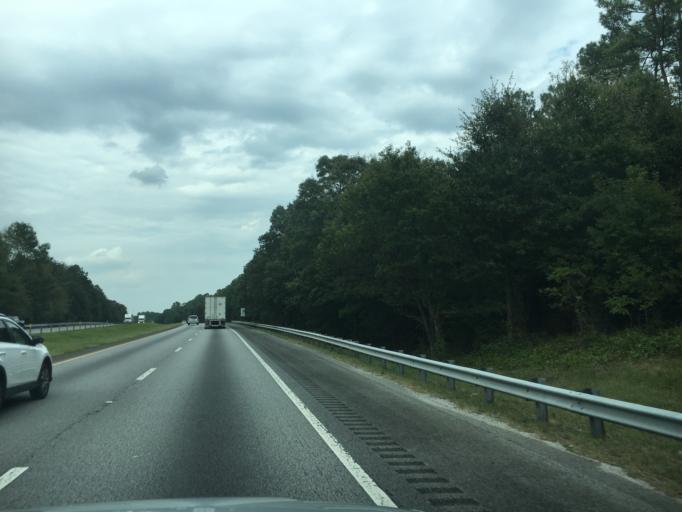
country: US
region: Georgia
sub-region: Hart County
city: Reed Creek
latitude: 34.5288
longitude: -82.8385
